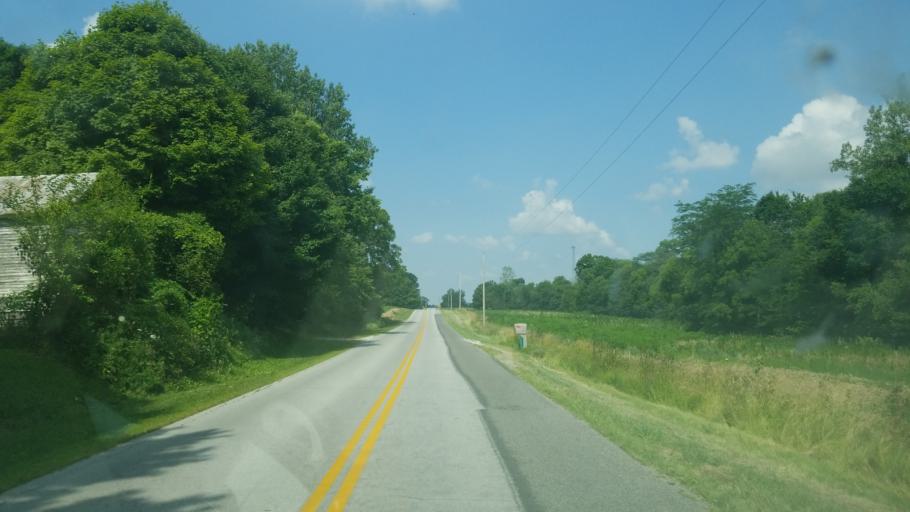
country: US
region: Ohio
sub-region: Auglaize County
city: Cridersville
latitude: 40.5712
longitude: -84.0717
